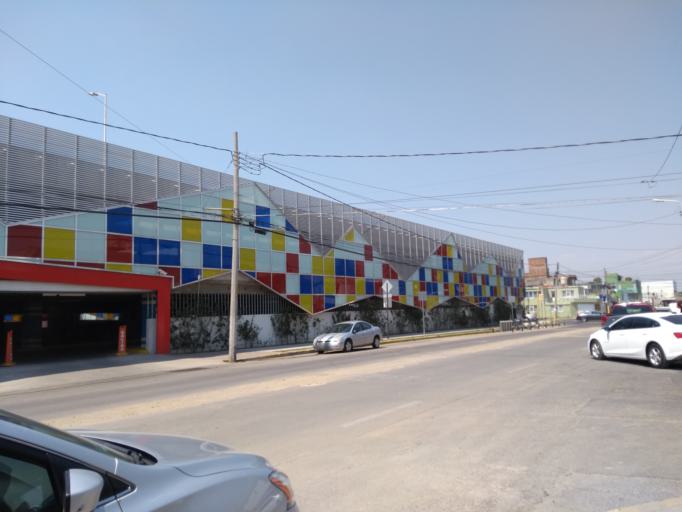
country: MX
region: Puebla
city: Puebla
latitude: 19.0121
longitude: -98.2019
